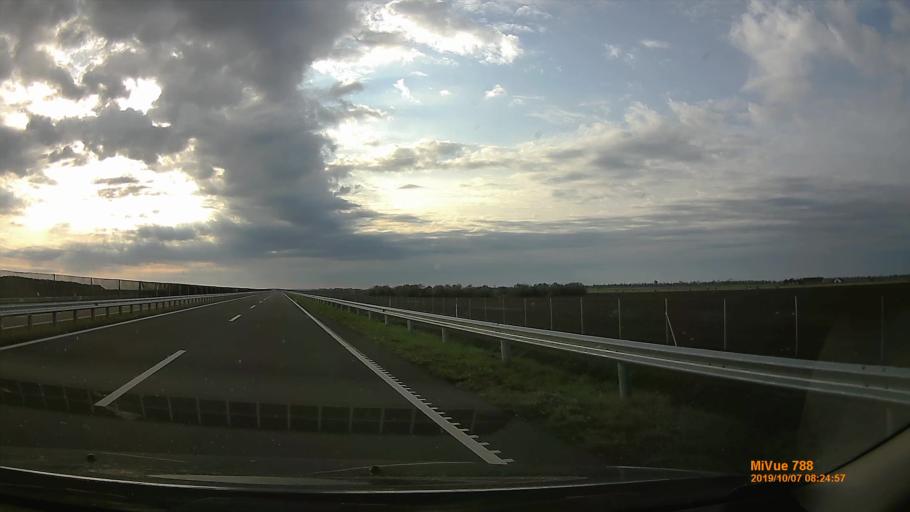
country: HU
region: Jasz-Nagykun-Szolnok
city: Kunszentmarton
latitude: 46.8340
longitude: 20.3489
